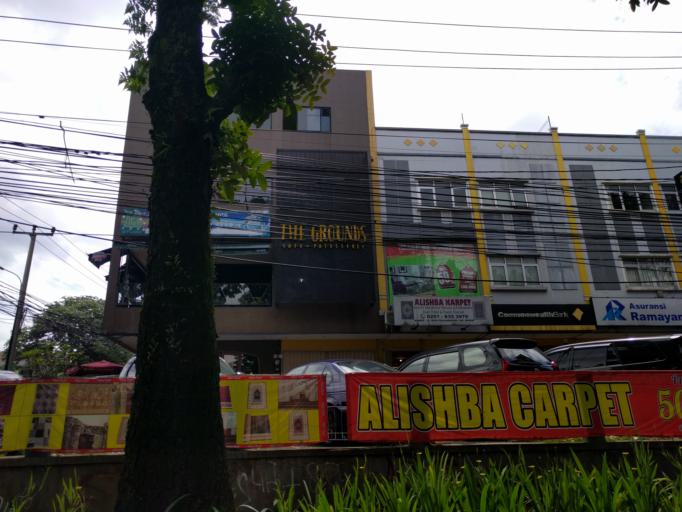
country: ID
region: West Java
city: Bogor
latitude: -6.6126
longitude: 106.8132
